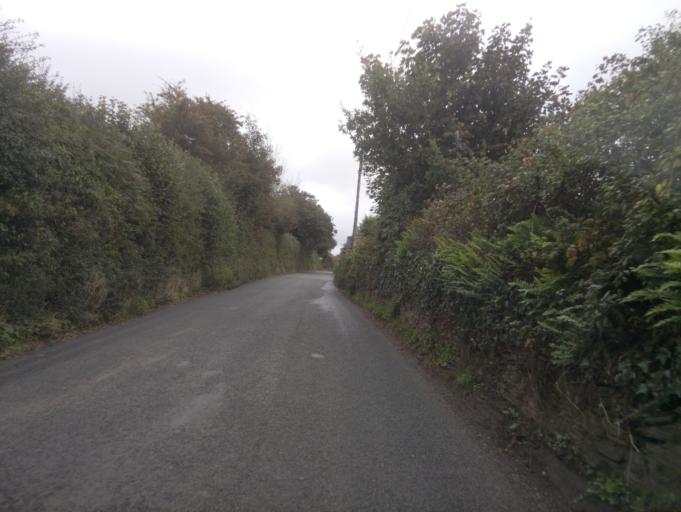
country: GB
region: England
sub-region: Devon
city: Salcombe
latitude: 50.2731
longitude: -3.6877
